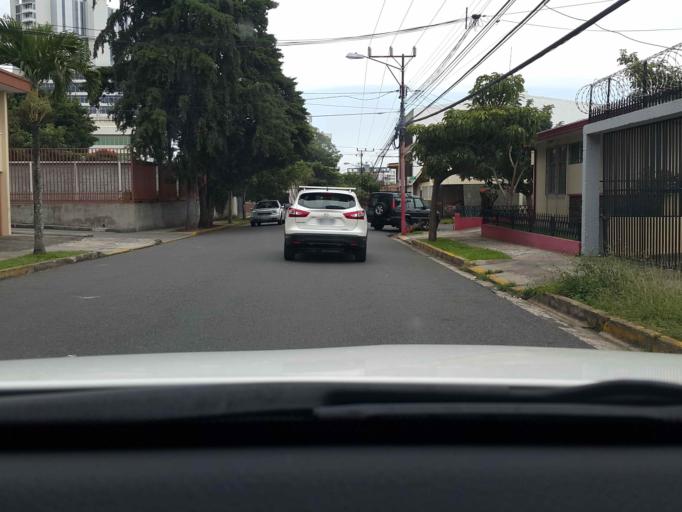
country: CR
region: San Jose
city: San Jose
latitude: 9.9396
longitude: -84.1066
